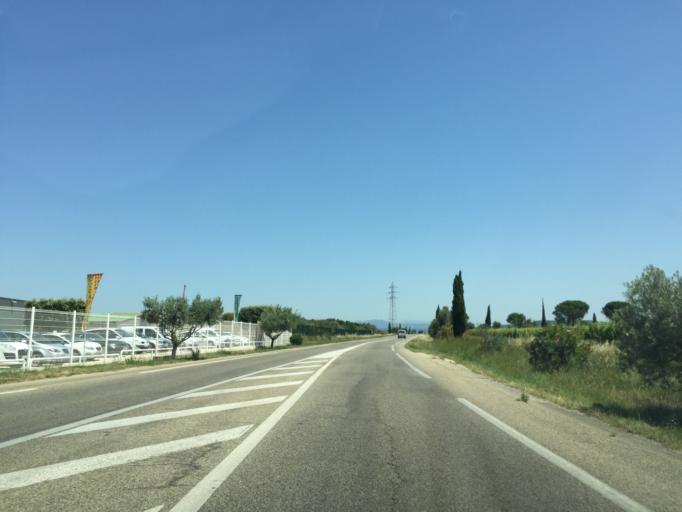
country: FR
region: Provence-Alpes-Cote d'Azur
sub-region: Departement du Vaucluse
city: Sainte-Cecile-les-Vignes
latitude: 44.2139
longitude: 4.8696
